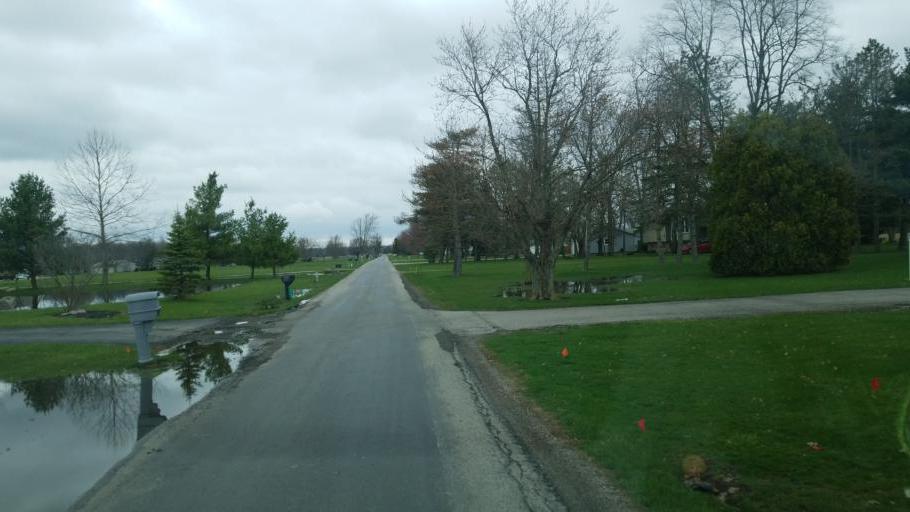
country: US
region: Ohio
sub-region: Marion County
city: Prospect
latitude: 40.4853
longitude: -83.1176
